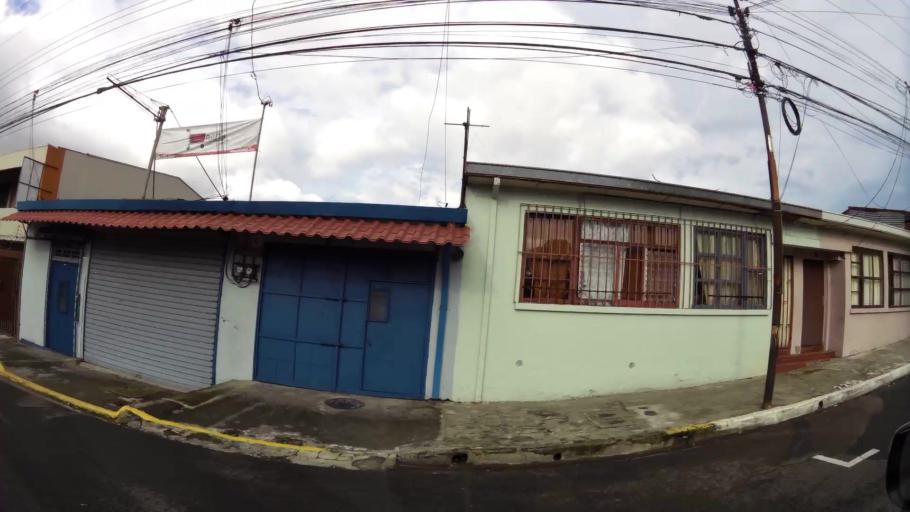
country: CR
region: San Jose
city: San Jose
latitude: 9.9388
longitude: -84.0881
